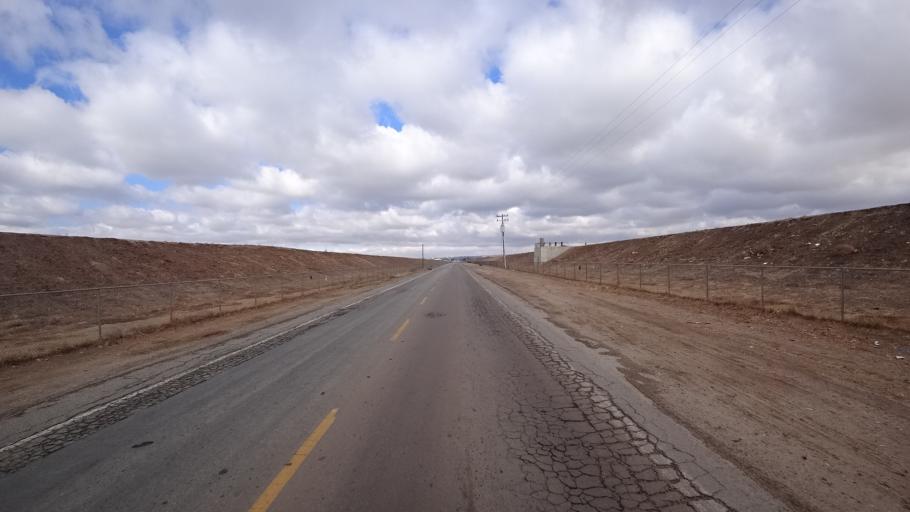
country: US
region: California
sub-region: Kern County
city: Bakersfield
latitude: 35.3297
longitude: -118.9677
